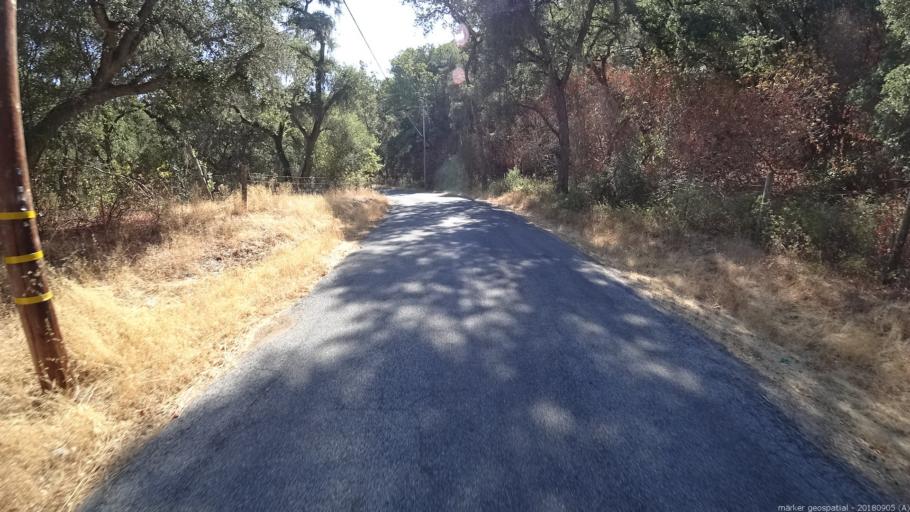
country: US
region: California
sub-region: Monterey County
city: Carmel Valley Village
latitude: 36.3951
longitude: -121.6468
